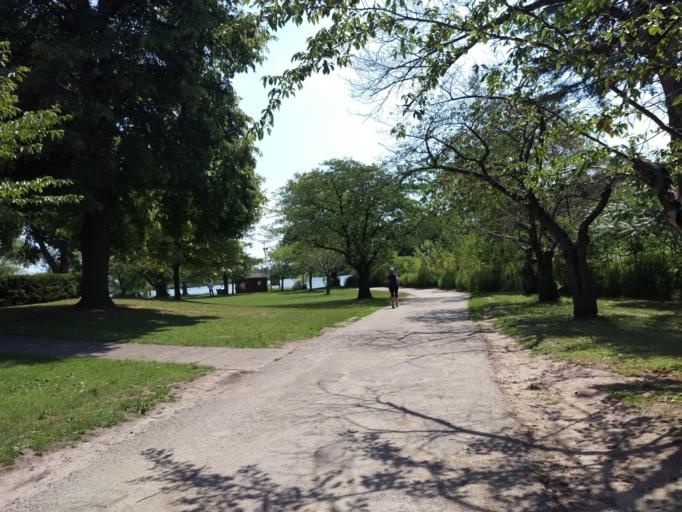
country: CA
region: Ontario
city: Toronto
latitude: 43.6434
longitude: -79.4672
